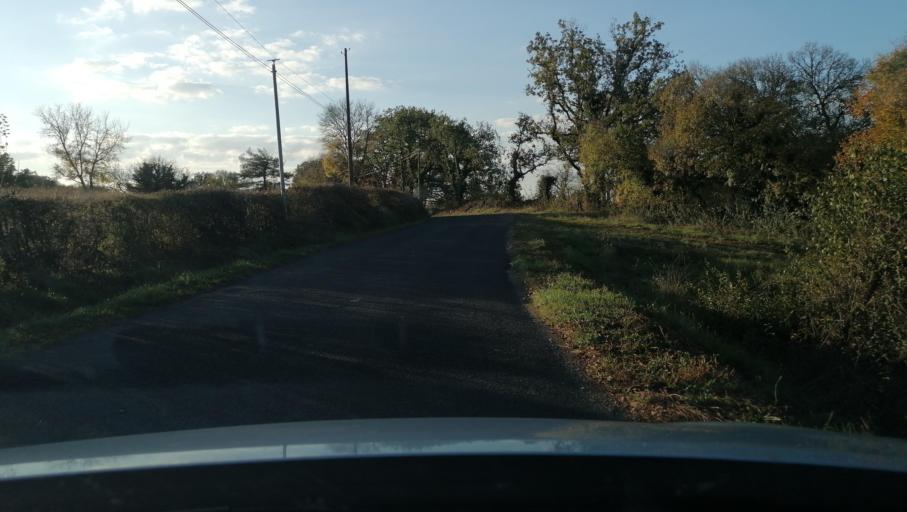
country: FR
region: Midi-Pyrenees
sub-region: Departement du Lot
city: Vayrac
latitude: 44.8708
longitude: 1.6456
